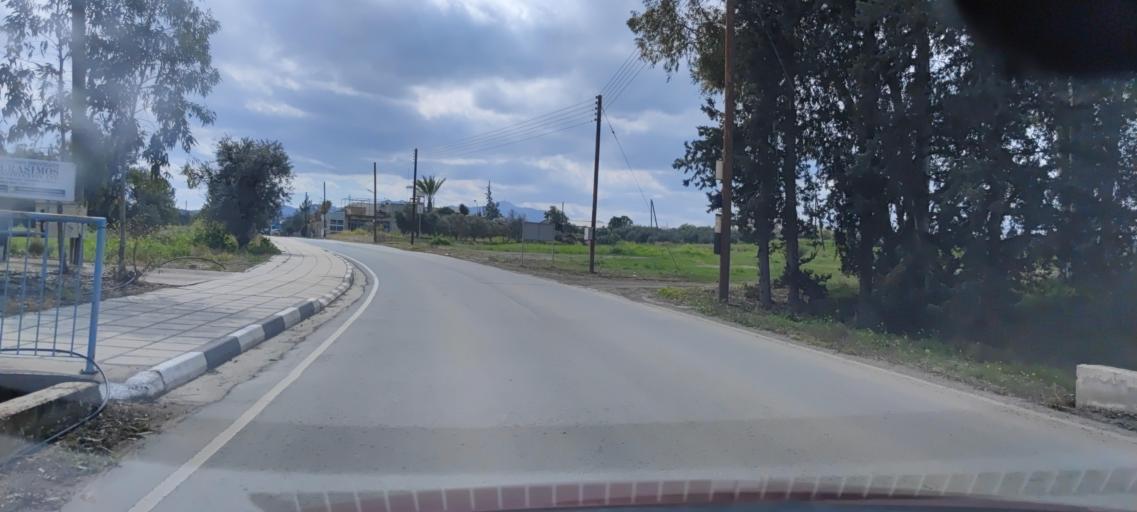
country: CY
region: Lefkosia
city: Pera
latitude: 35.0141
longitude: 33.2932
